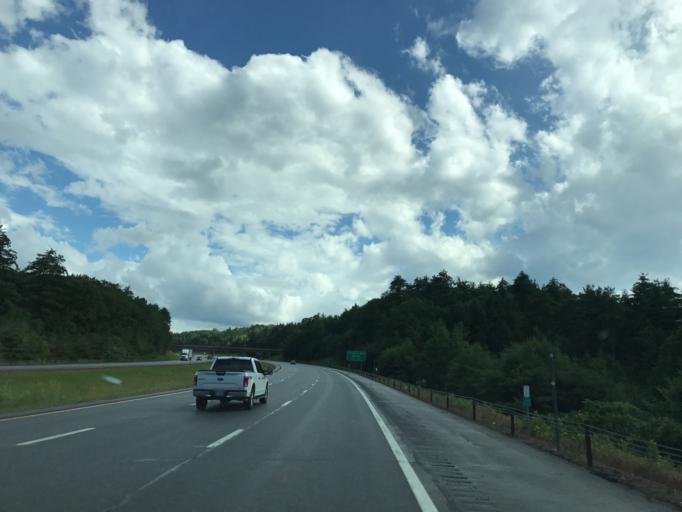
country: US
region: New York
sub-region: Warren County
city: Glens Falls North
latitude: 43.4146
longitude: -73.7232
